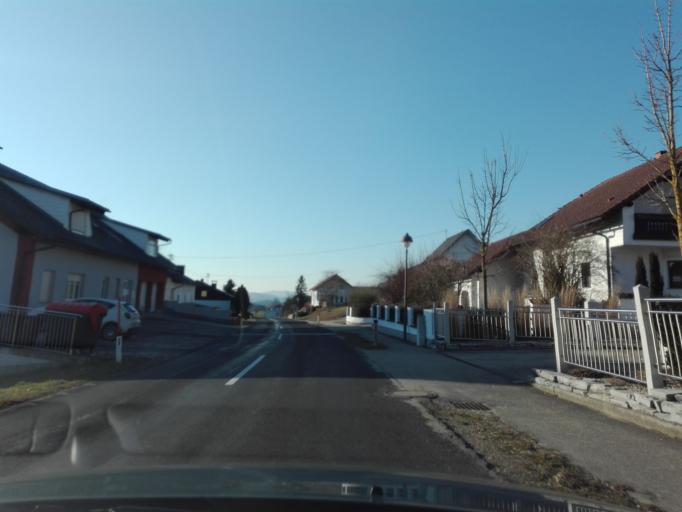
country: AT
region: Upper Austria
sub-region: Politischer Bezirk Rohrbach
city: Kleinzell im Muehlkreis
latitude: 48.4036
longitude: 13.9258
